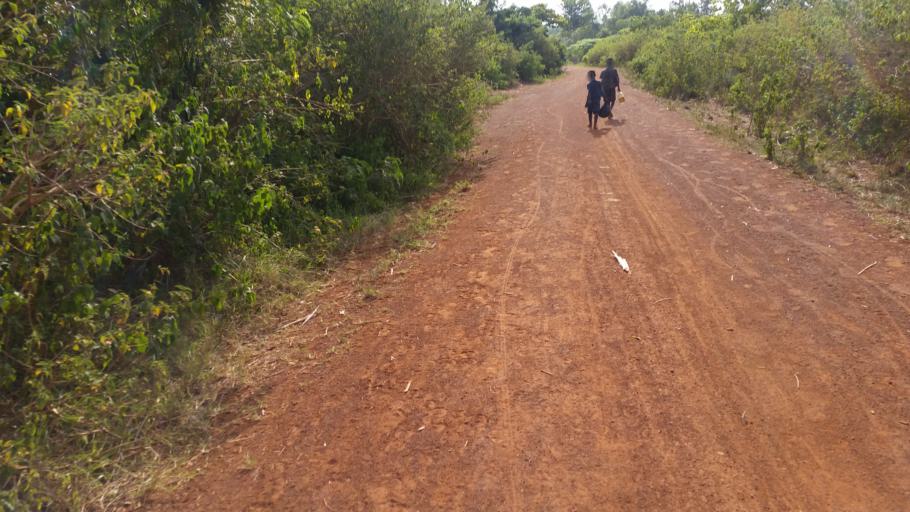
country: UG
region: Eastern Region
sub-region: Busia District
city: Busia
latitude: 0.5498
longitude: 34.0015
